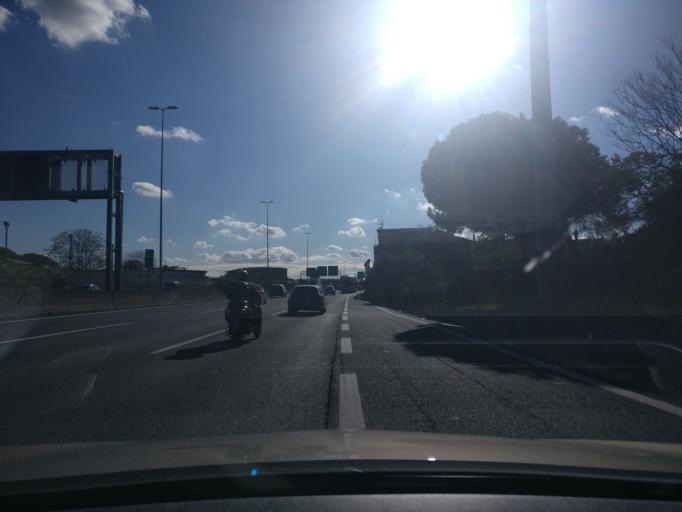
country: IT
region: Latium
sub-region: Citta metropolitana di Roma Capitale
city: Ciampino
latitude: 41.8480
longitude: 12.5956
